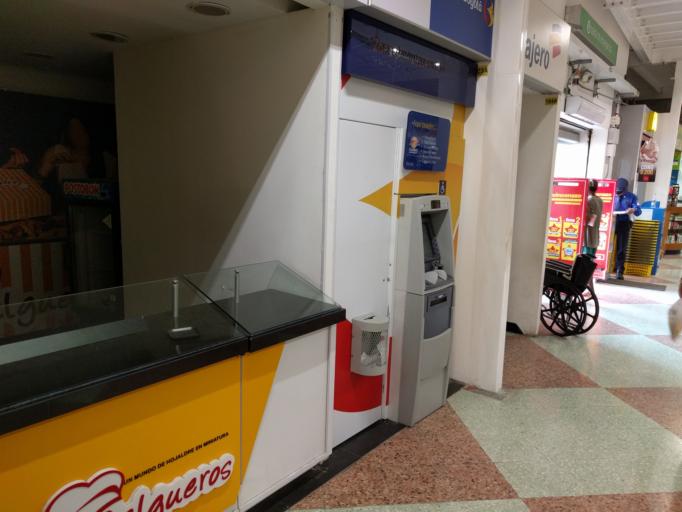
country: CO
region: Bolivar
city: Cartagena
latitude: 10.4276
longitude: -75.5454
